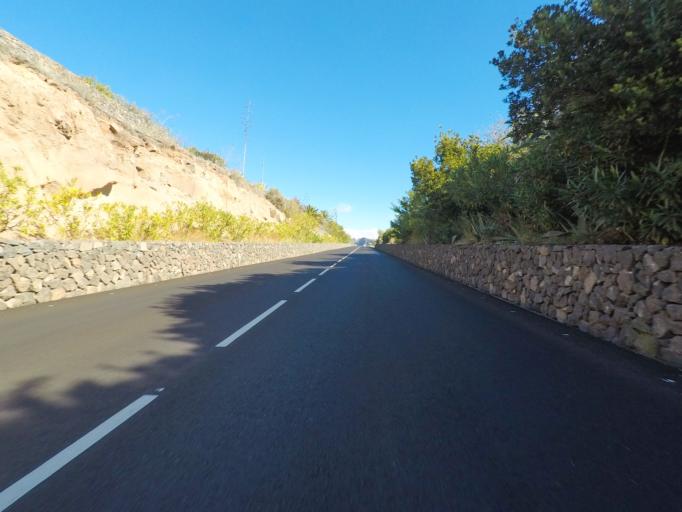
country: ES
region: Canary Islands
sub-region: Provincia de Santa Cruz de Tenerife
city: Alajero
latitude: 28.0413
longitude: -17.1948
